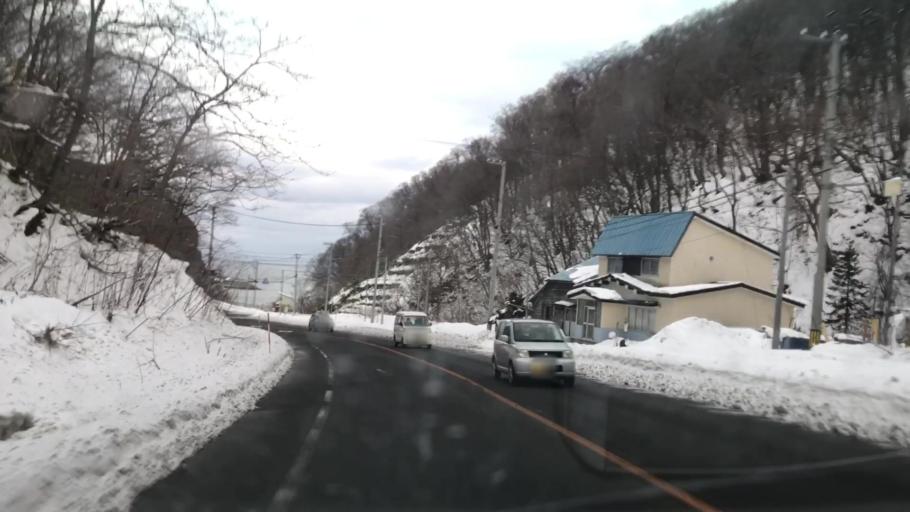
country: JP
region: Hokkaido
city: Yoichi
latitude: 43.2314
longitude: 140.7359
